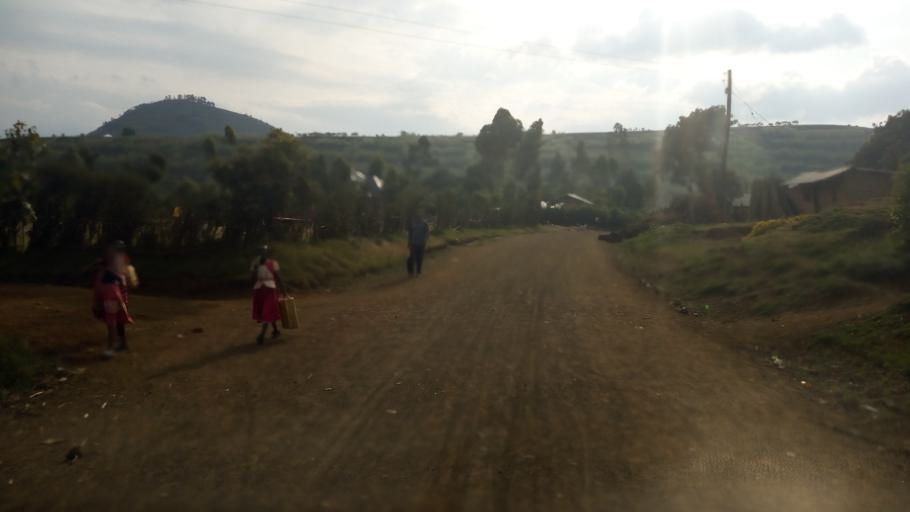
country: UG
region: Western Region
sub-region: Kisoro District
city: Kisoro
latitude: -1.3024
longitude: 29.7044
